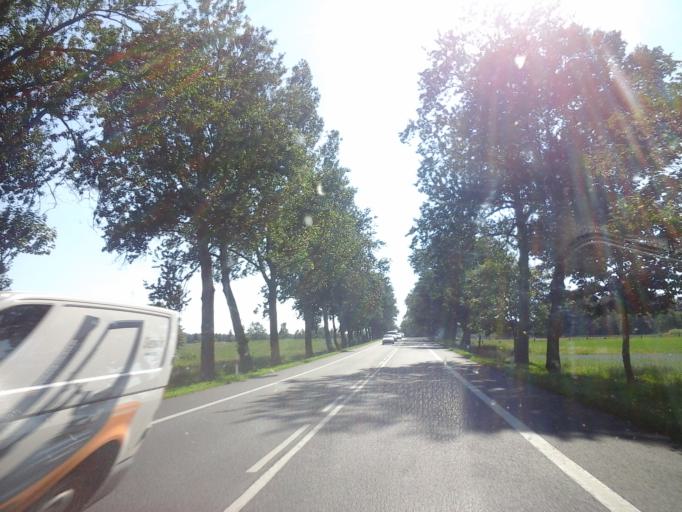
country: PL
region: West Pomeranian Voivodeship
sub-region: Powiat kolobrzeski
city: Ryman
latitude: 53.9535
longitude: 15.5544
